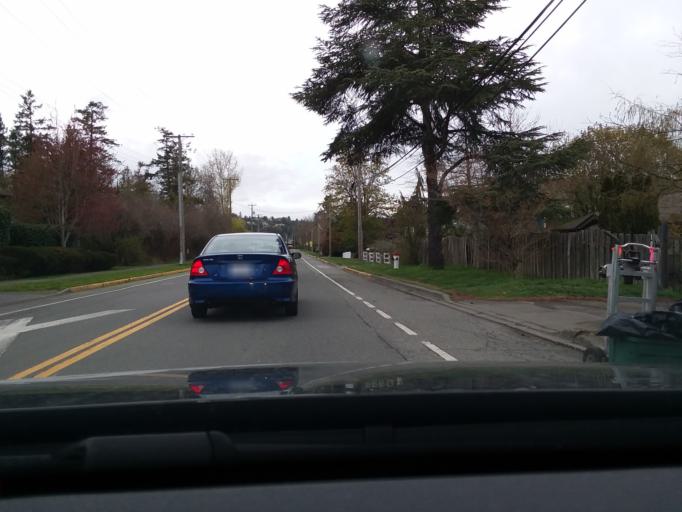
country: CA
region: British Columbia
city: North Saanich
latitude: 48.6679
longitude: -123.4173
